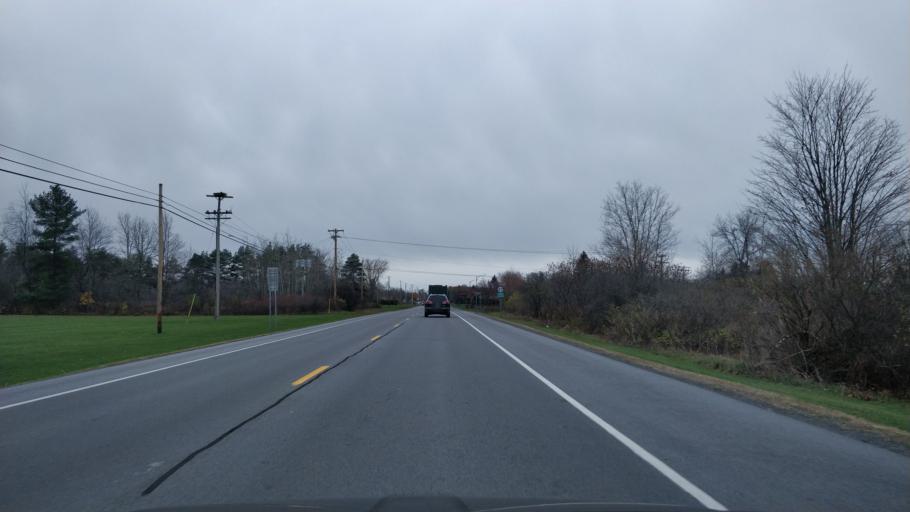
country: CA
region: Ontario
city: Prescott
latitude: 44.6670
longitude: -75.5363
